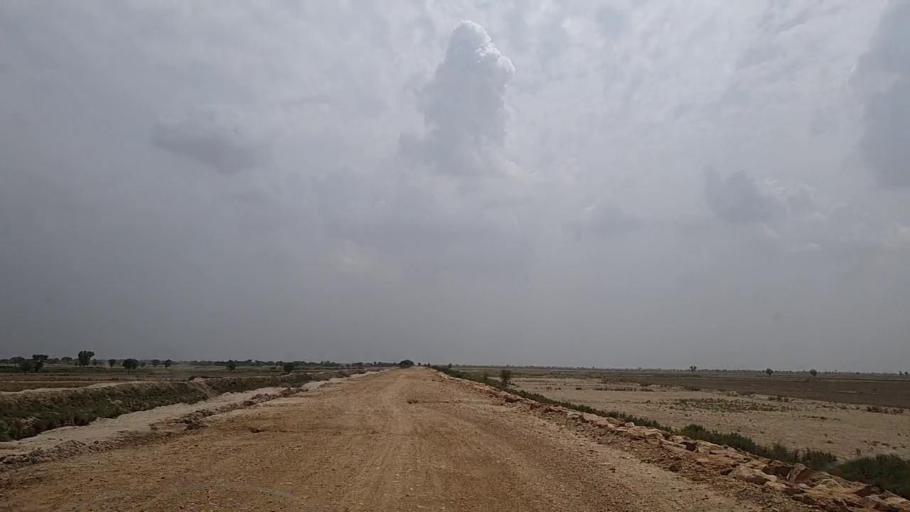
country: PK
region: Sindh
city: Johi
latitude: 26.7456
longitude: 67.5879
